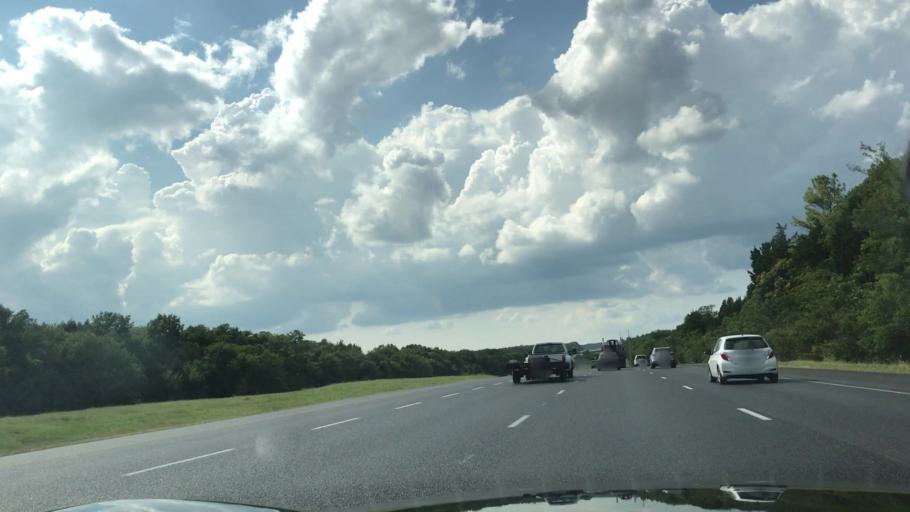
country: US
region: Tennessee
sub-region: Rutherford County
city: Smyrna
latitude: 35.9434
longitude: -86.5412
